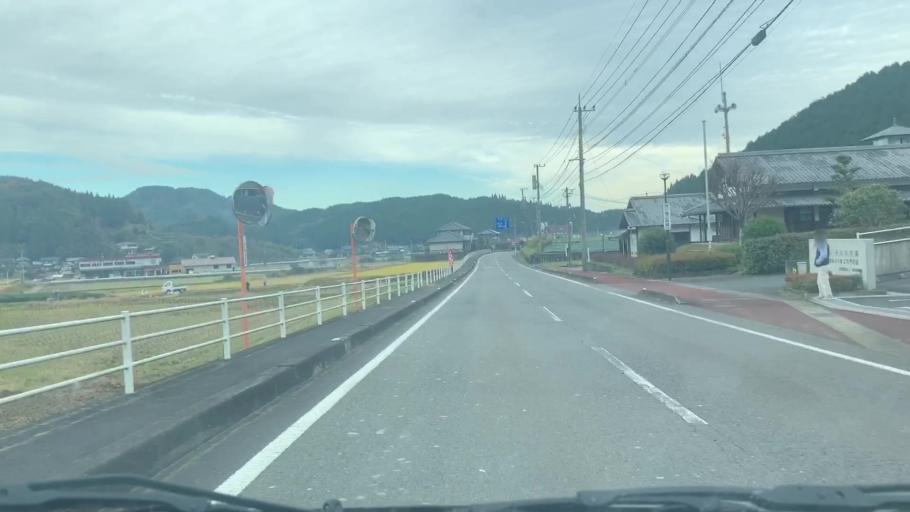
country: JP
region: Saga Prefecture
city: Ureshinomachi-shimojuku
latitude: 33.1347
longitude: 129.9744
